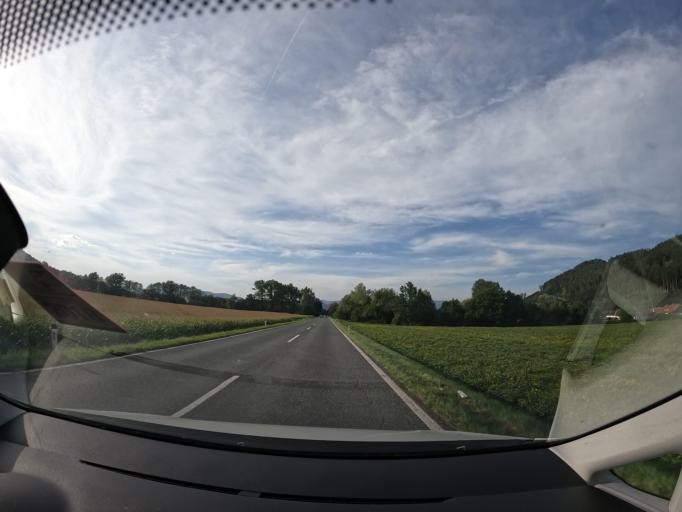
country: AT
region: Carinthia
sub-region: Politischer Bezirk Volkermarkt
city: Eberndorf
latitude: 46.5958
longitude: 14.6346
